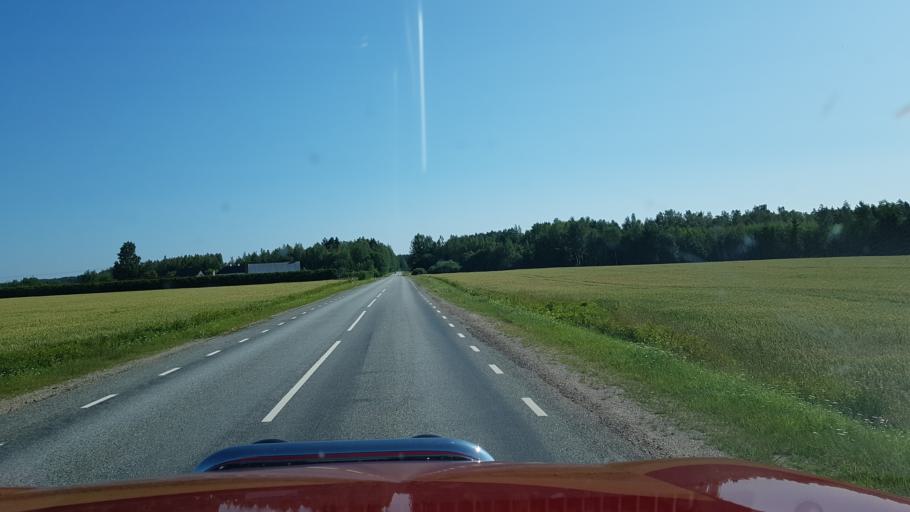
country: EE
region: Polvamaa
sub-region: Polva linn
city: Polva
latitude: 58.0007
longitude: 26.9320
